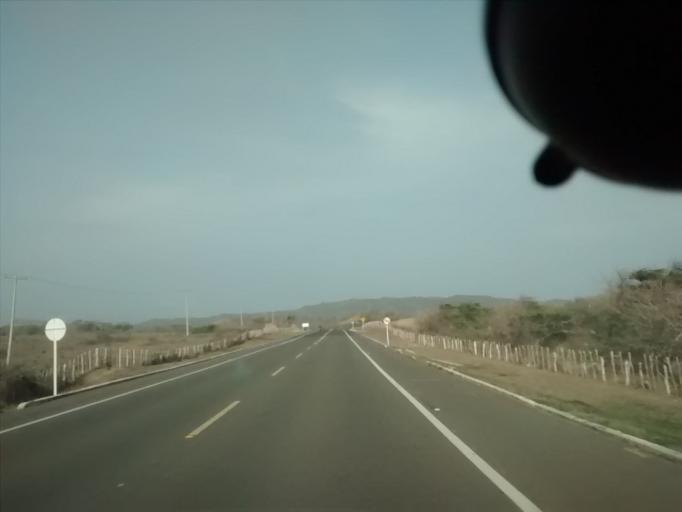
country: CO
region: Atlantico
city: Juan de Acosta
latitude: 10.8600
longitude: -75.1148
